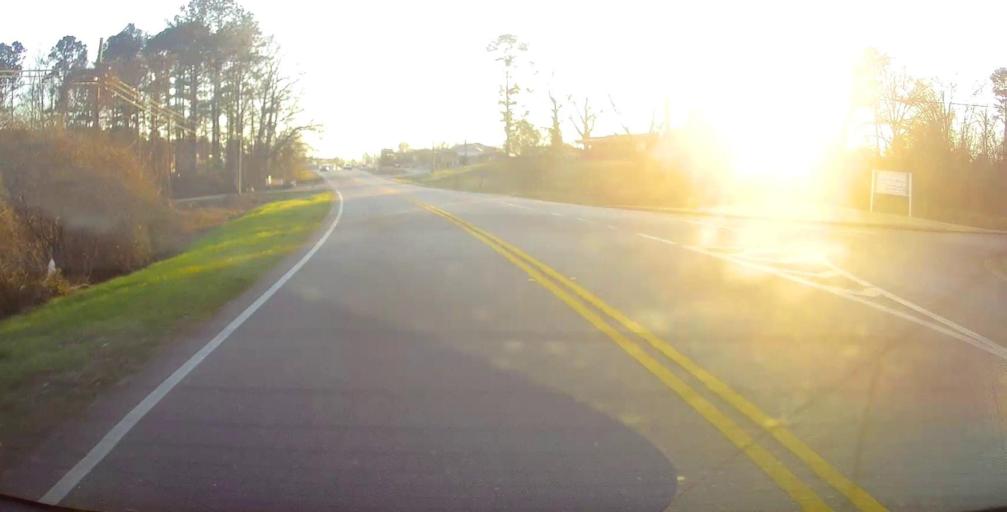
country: US
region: Georgia
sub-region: Troup County
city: La Grange
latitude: 33.0263
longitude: -85.0761
